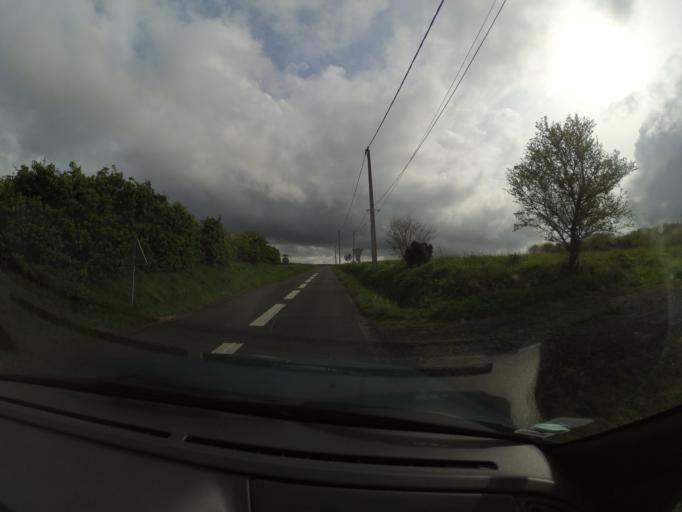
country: FR
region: Pays de la Loire
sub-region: Departement de la Loire-Atlantique
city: Maisdon-sur-Sevre
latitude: 47.1103
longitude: -1.3612
